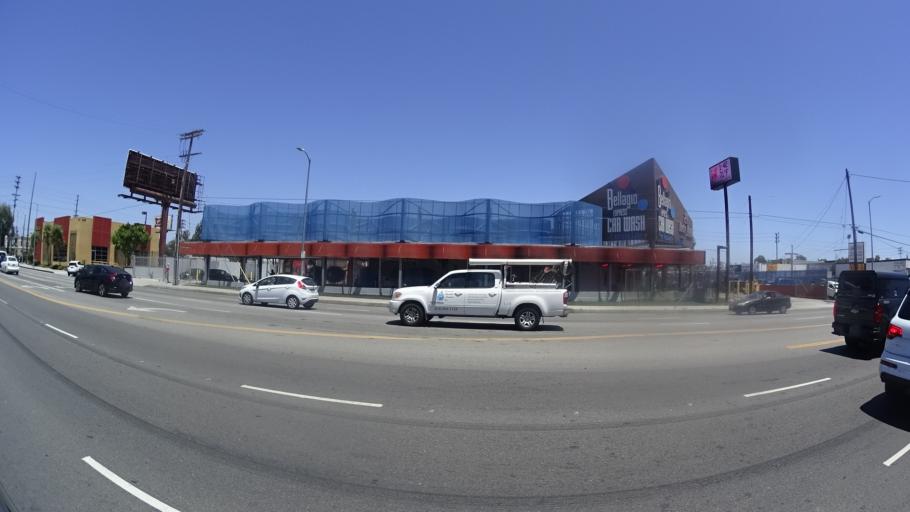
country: US
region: California
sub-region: Los Angeles County
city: Van Nuys
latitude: 34.1859
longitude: -118.4662
